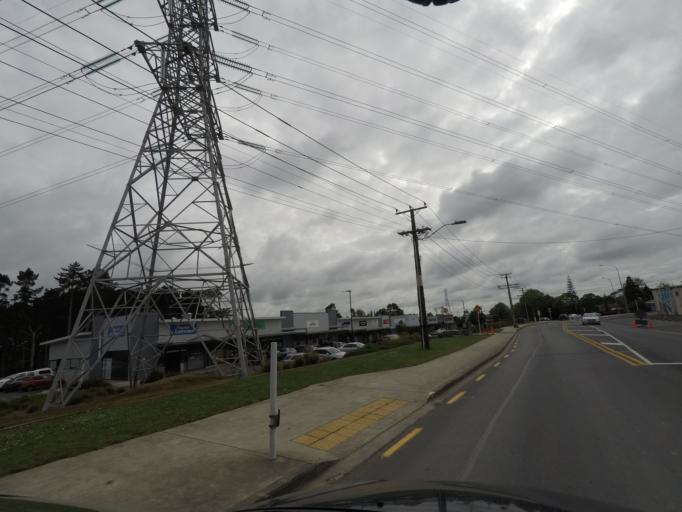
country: NZ
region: Auckland
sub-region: Auckland
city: Rosebank
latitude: -36.8370
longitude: 174.6000
